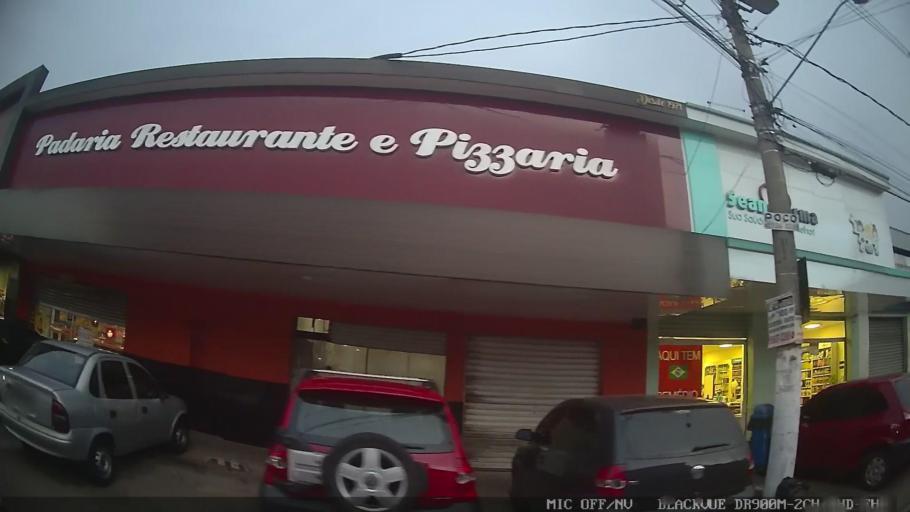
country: BR
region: Sao Paulo
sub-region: Suzano
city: Suzano
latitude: -23.6446
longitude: -46.3223
